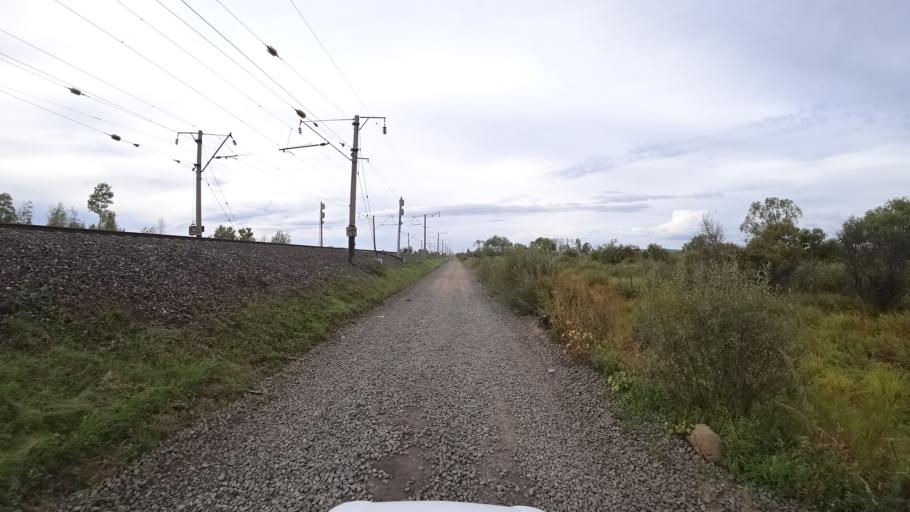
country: RU
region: Amur
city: Arkhara
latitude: 49.3571
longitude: 130.1530
